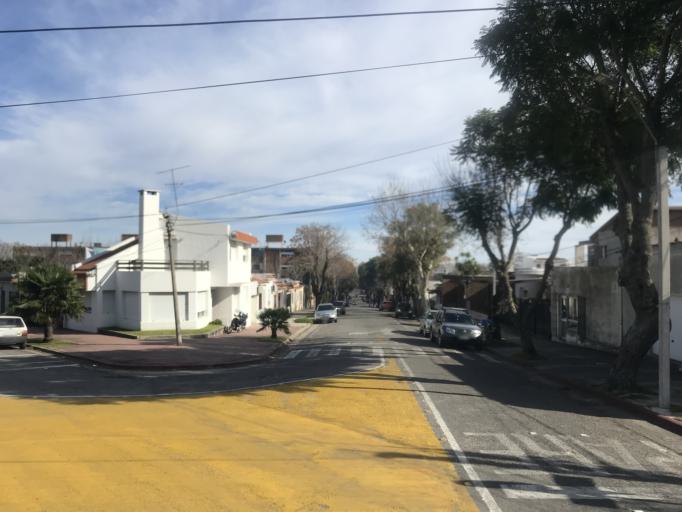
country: UY
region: Colonia
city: Colonia del Sacramento
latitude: -34.4675
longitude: -57.8384
